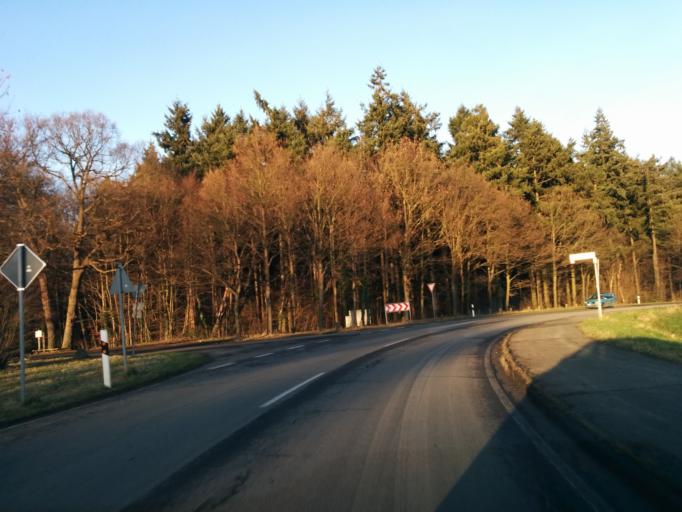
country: DE
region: North Rhine-Westphalia
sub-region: Regierungsbezirk Koln
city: Rheinbach
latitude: 50.6043
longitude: 6.9338
